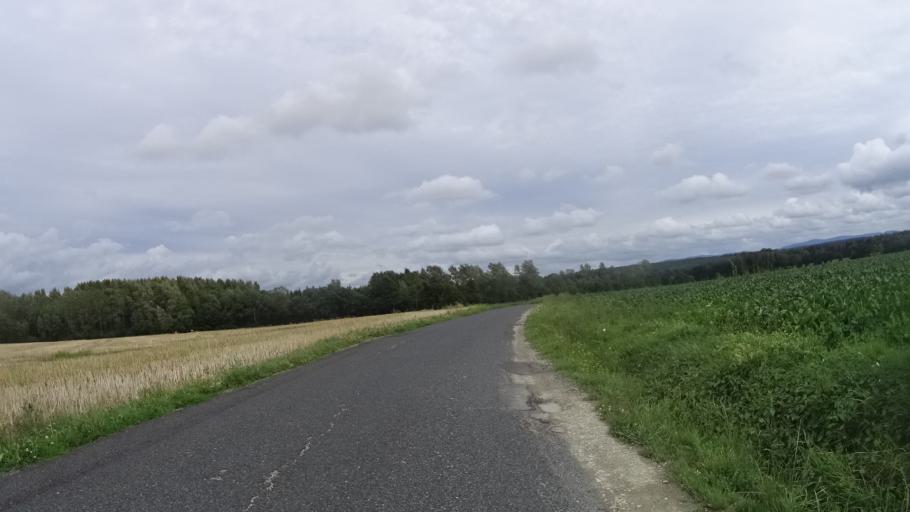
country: FR
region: Lorraine
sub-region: Departement de la Moselle
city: Sarrebourg
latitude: 48.6965
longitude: 7.0611
